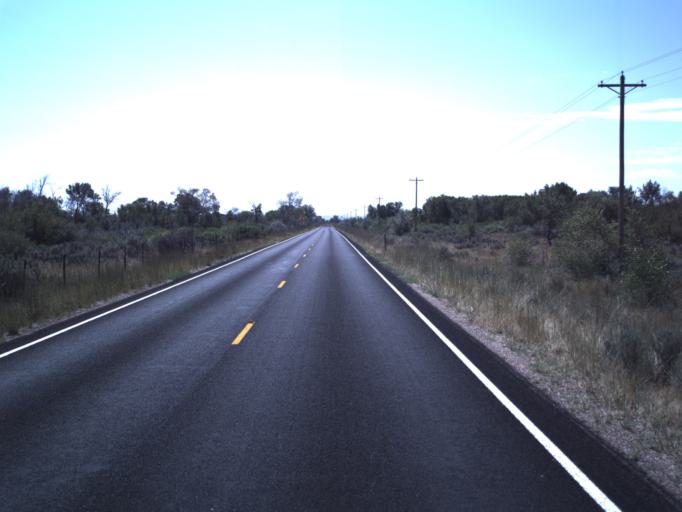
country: US
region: Utah
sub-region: Duchesne County
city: Roosevelt
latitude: 40.4235
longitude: -109.9235
